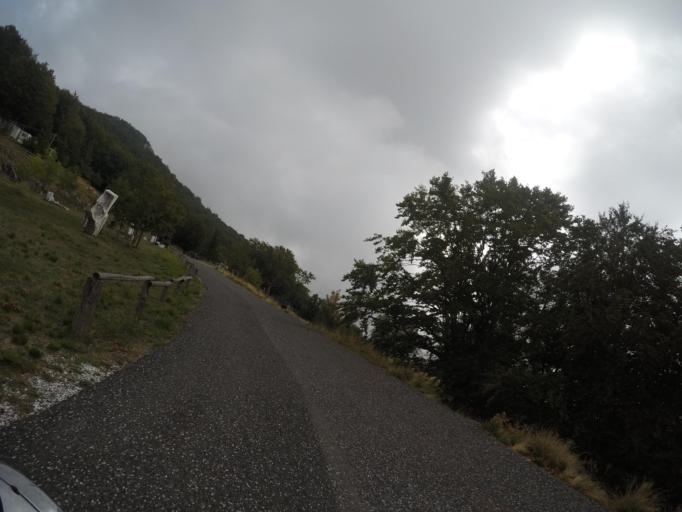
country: IT
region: Tuscany
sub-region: Provincia di Massa-Carrara
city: Carrara
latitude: 44.1215
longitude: 10.1205
